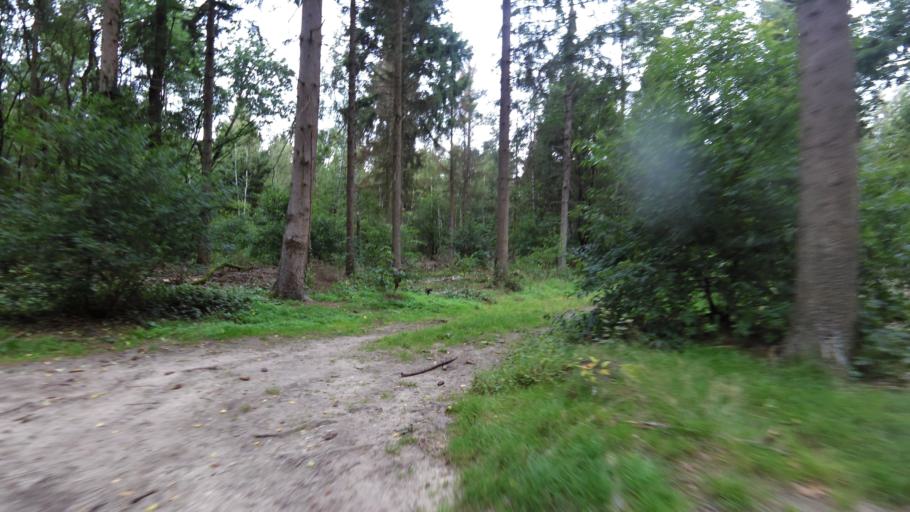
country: NL
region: Gelderland
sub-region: Gemeente Ede
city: Bennekom
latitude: 52.0032
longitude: 5.6923
